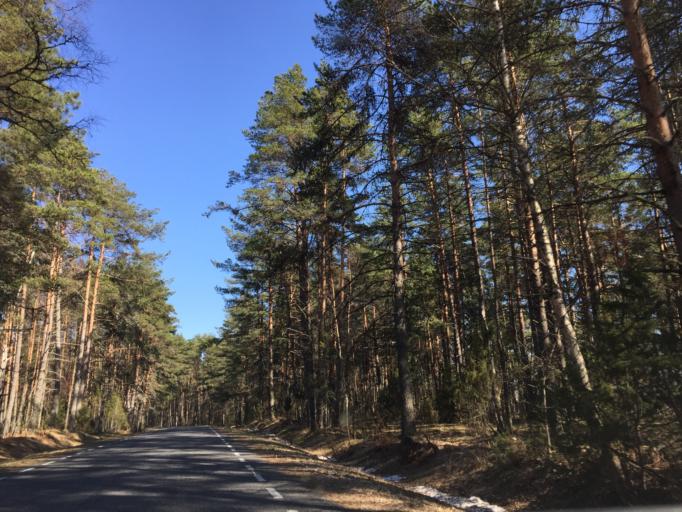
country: EE
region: Ida-Virumaa
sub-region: Johvi vald
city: Johvi
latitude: 59.0073
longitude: 27.4125
